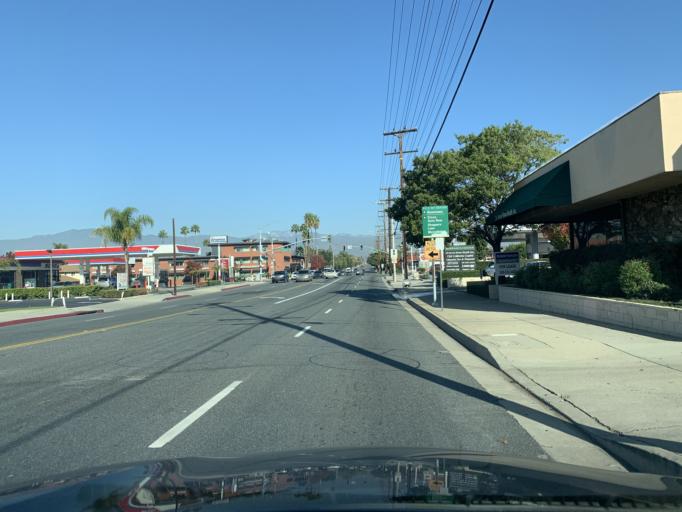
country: US
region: California
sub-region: Los Angeles County
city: Covina
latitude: 34.0780
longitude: -117.8813
